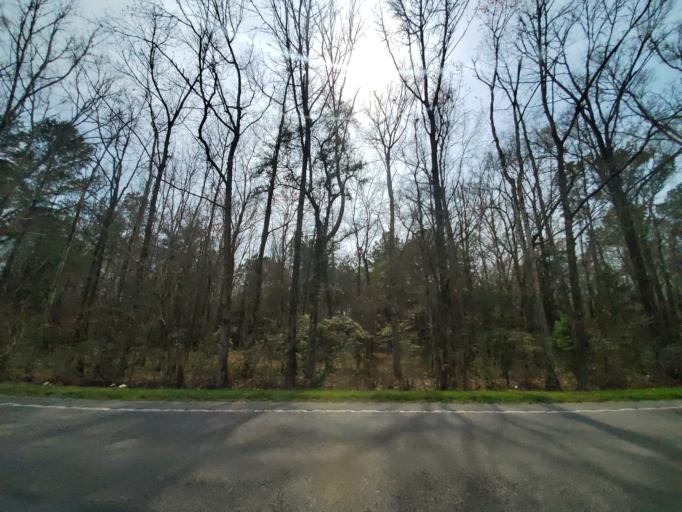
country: US
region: South Carolina
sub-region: Dorchester County
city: Centerville
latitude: 32.9649
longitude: -80.2918
